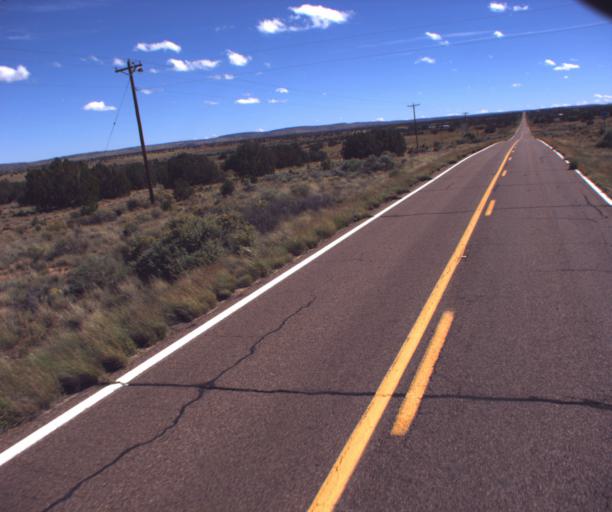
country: US
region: Arizona
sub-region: Apache County
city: Saint Johns
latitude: 34.6140
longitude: -109.6599
